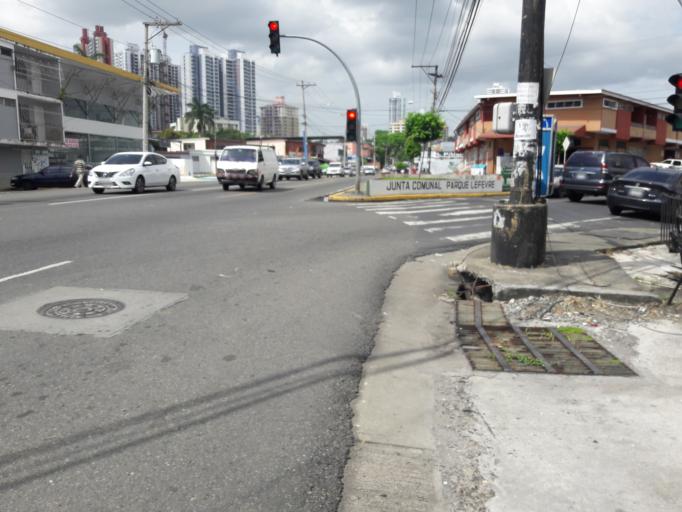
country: PA
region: Panama
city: Panama
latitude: 9.0074
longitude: -79.5034
